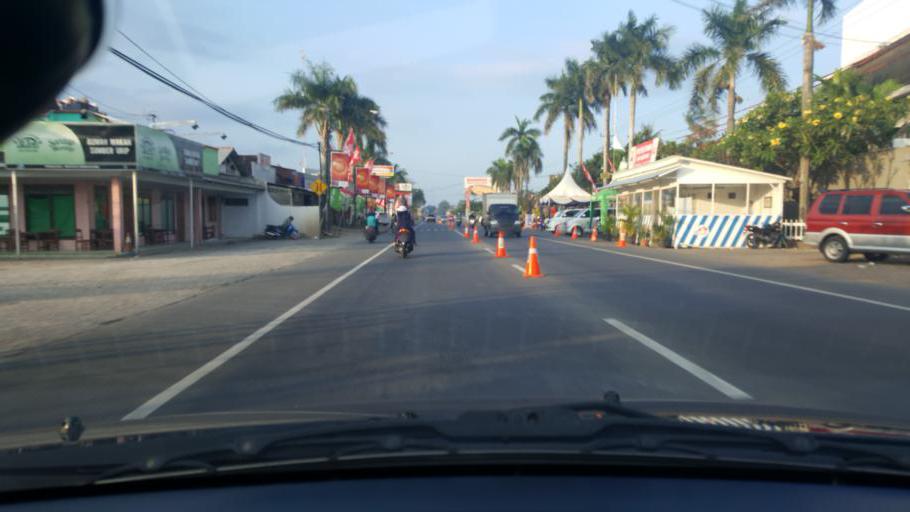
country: ID
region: Central Java
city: Gemiring
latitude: -6.7820
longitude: 110.9879
